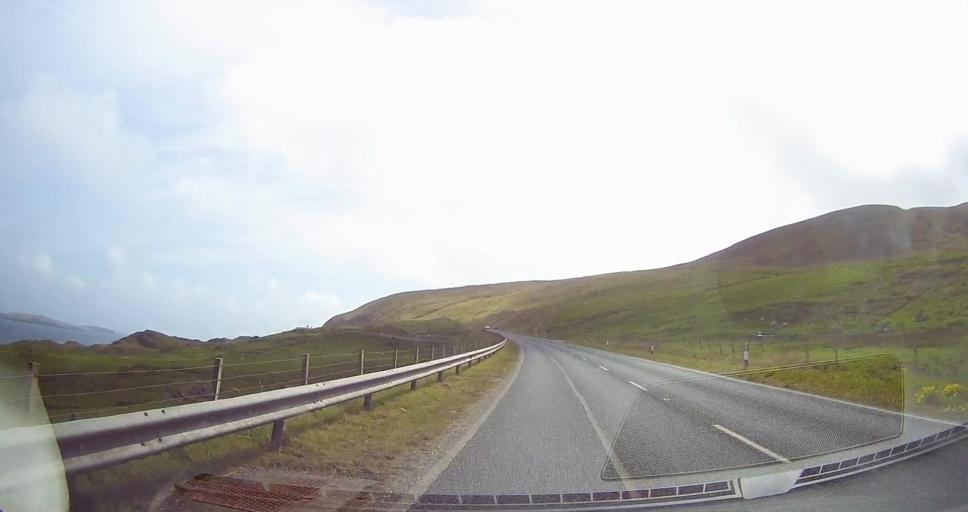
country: GB
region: Scotland
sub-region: Shetland Islands
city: Sandwick
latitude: 60.0282
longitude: -1.2359
